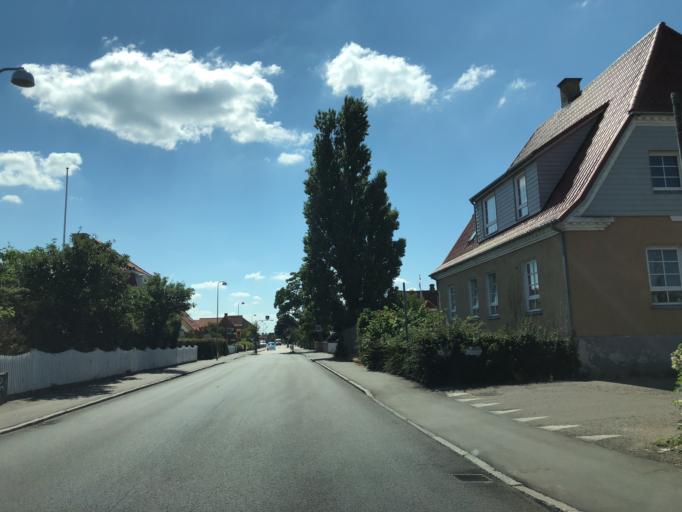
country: DK
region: Capital Region
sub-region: Halsnaes Kommune
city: Hundested
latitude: 55.9578
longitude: 11.8534
